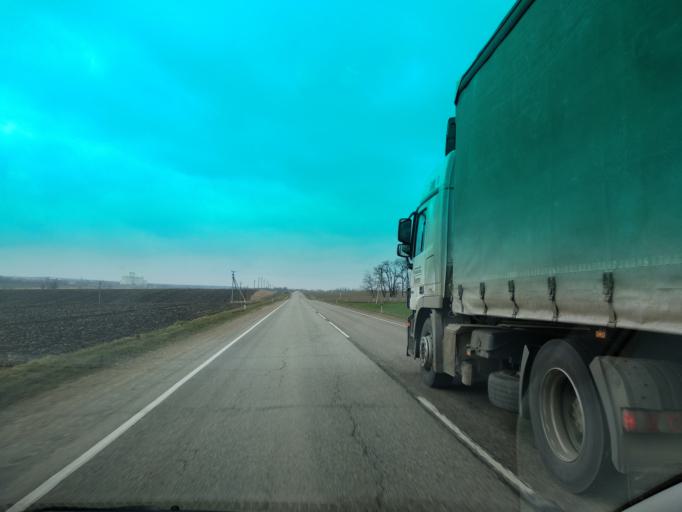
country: RU
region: Krasnodarskiy
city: Novomalorossiyskaya
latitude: 45.7166
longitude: 39.8791
